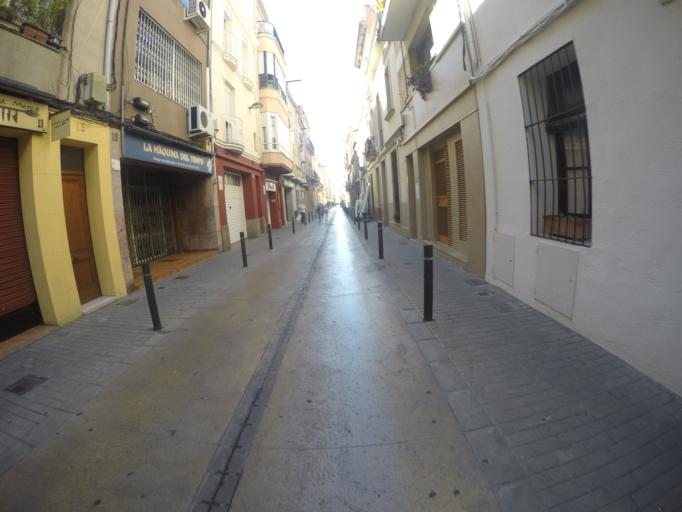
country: ES
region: Catalonia
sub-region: Provincia de Barcelona
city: Badalona
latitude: 41.4504
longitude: 2.2509
